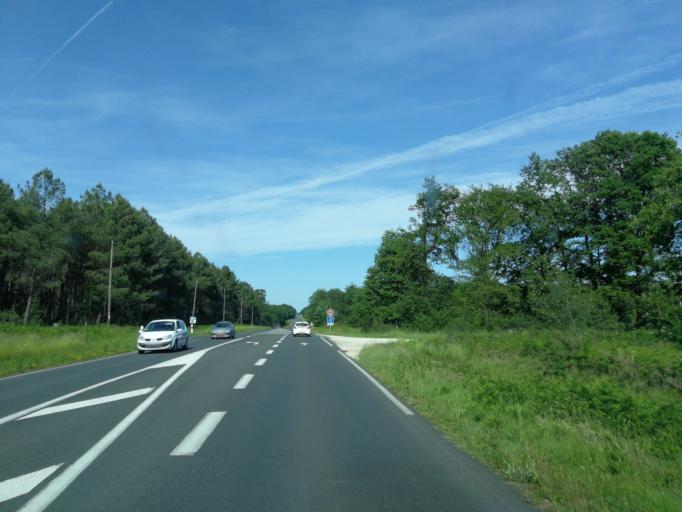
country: FR
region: Centre
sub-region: Departement d'Indre-et-Loire
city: Cheille
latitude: 47.2092
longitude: 0.3435
